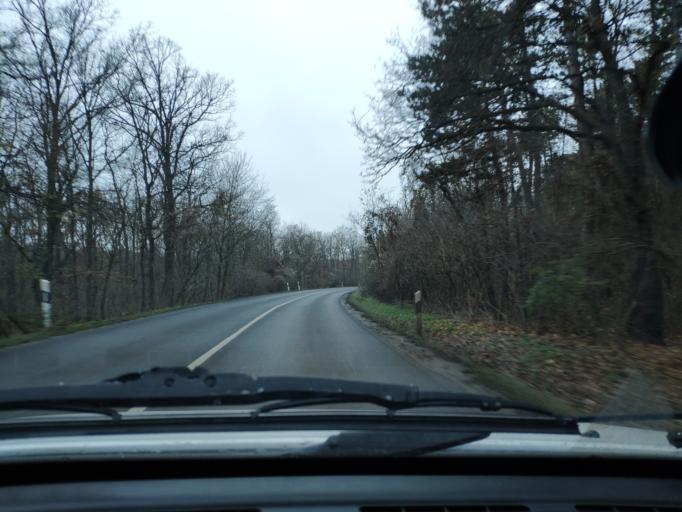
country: HU
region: Pest
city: Biatorbagy
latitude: 47.4387
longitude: 18.8185
